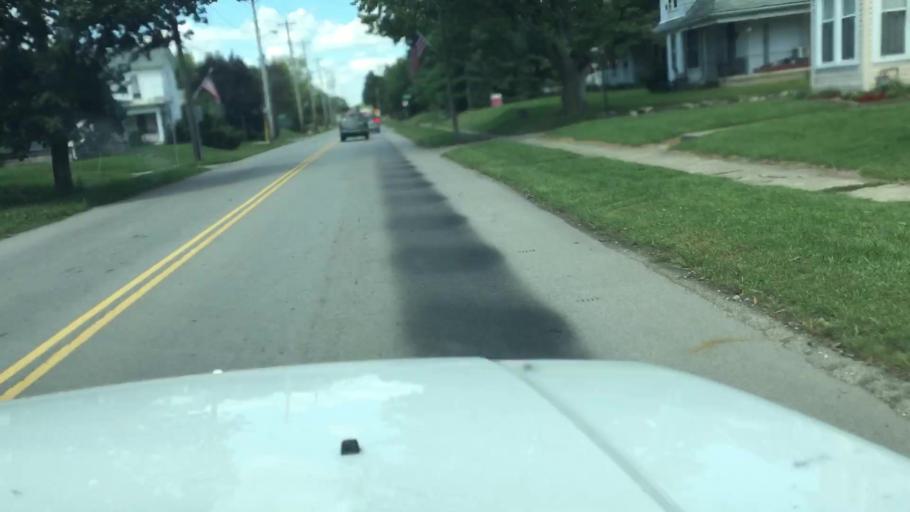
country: US
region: Ohio
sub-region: Madison County
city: Mount Sterling
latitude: 39.7230
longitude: -83.2685
